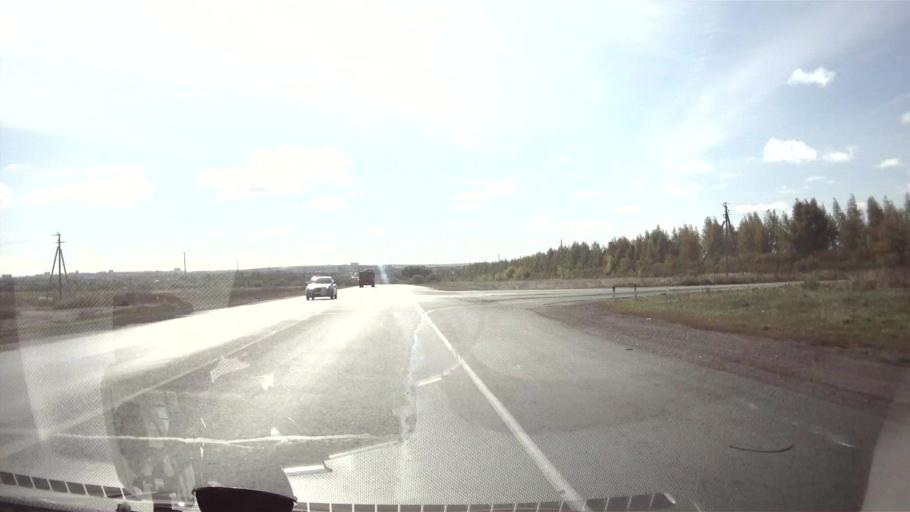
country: RU
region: Ulyanovsk
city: Isheyevka
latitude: 54.3118
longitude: 48.2357
